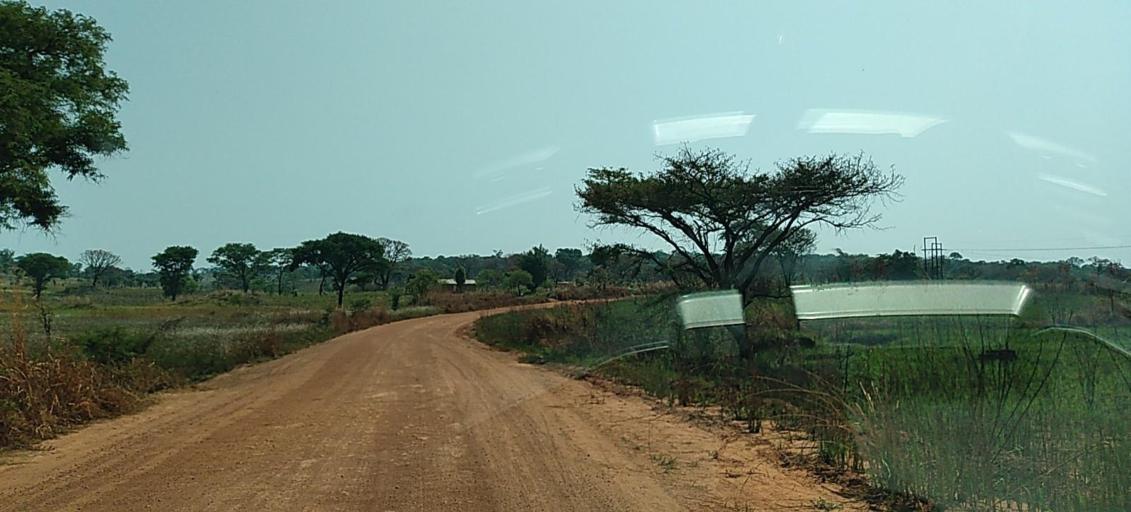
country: ZM
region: North-Western
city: Kansanshi
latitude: -12.0043
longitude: 26.5560
